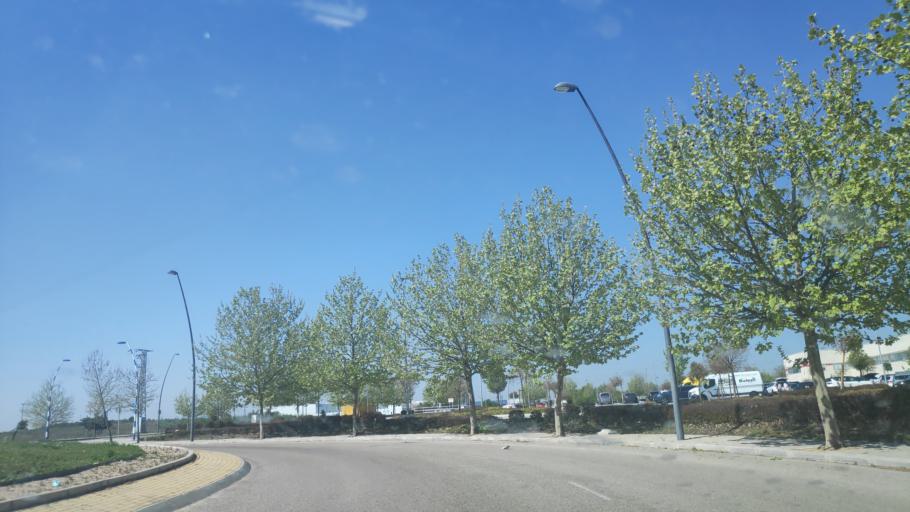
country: ES
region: Madrid
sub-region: Provincia de Madrid
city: Pinto
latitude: 40.2819
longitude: -3.6874
